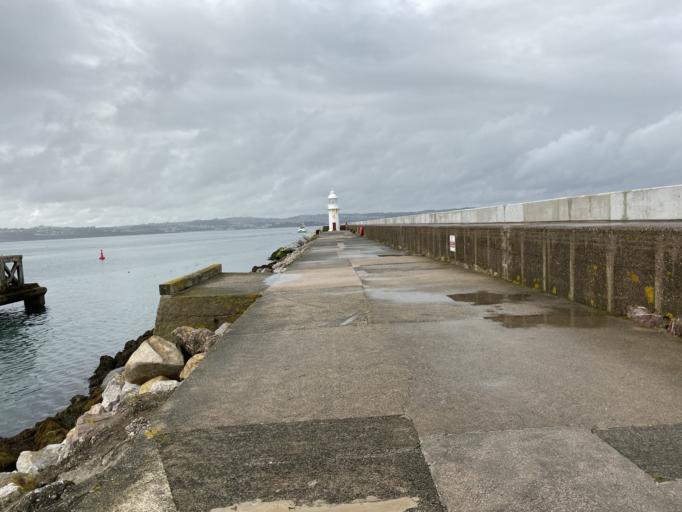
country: GB
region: England
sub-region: Borough of Torbay
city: Brixham
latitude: 50.4048
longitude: -3.5117
